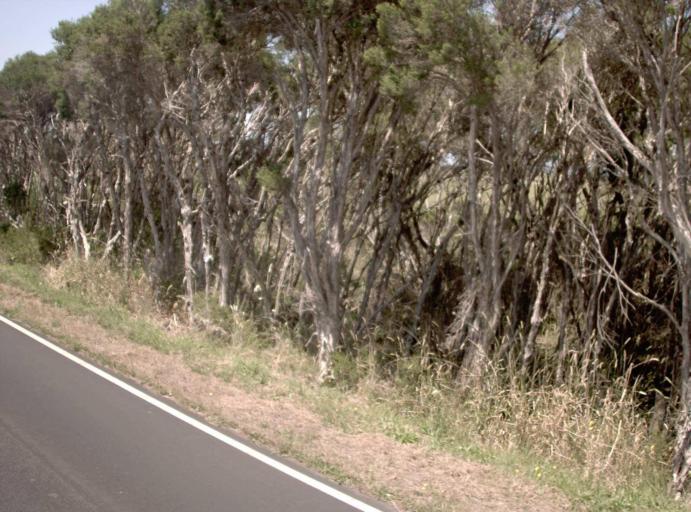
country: AU
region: Victoria
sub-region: Bass Coast
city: North Wonthaggi
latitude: -38.6376
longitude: 145.8458
